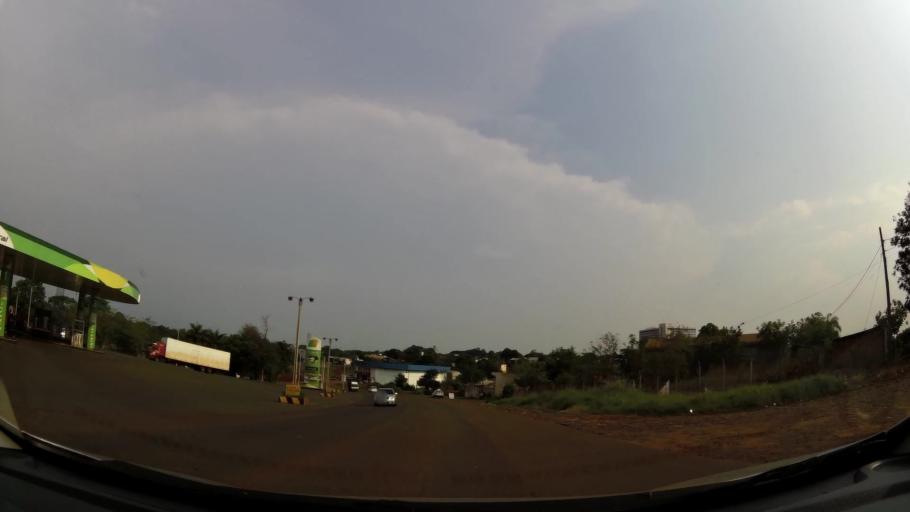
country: PY
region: Alto Parana
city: Ciudad del Este
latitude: -25.4904
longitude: -54.6635
